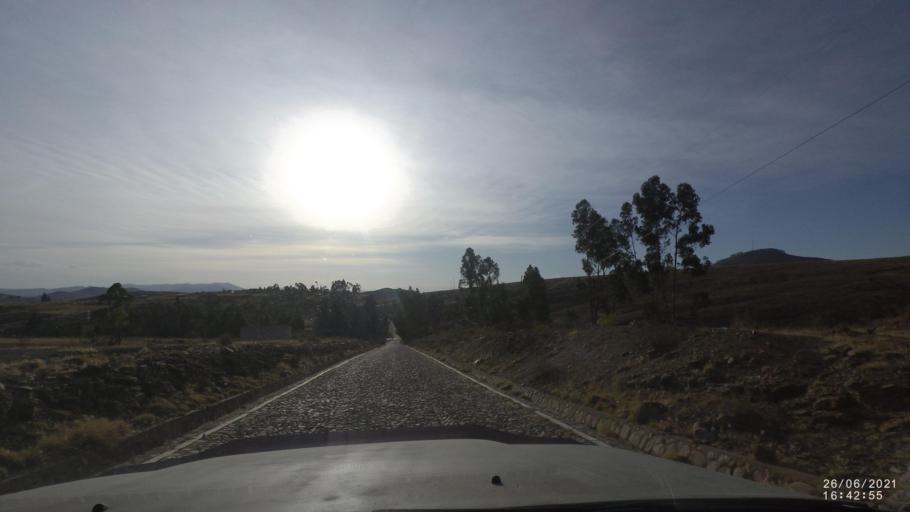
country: BO
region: Cochabamba
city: Arani
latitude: -17.7611
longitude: -65.8291
